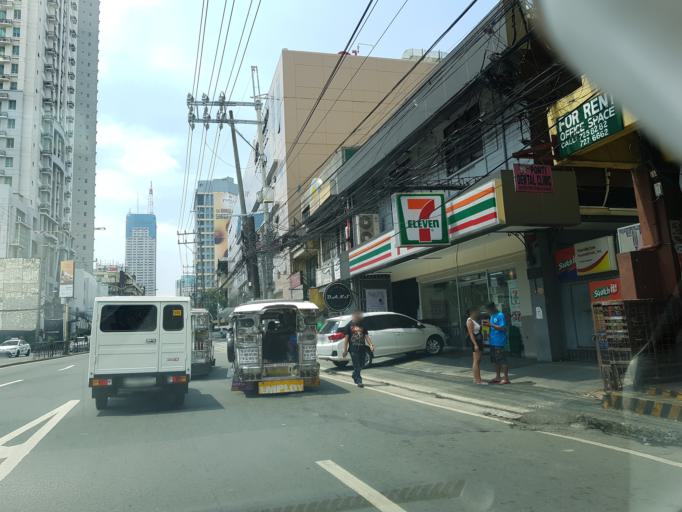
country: PH
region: Metro Manila
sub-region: Mandaluyong
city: Mandaluyong City
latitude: 14.5834
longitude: 121.0512
